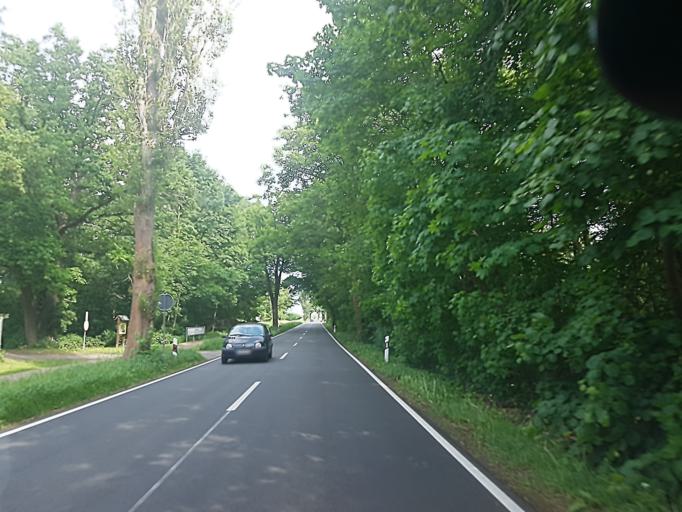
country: DE
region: Saxony-Anhalt
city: Coswig
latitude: 51.8990
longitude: 12.4382
